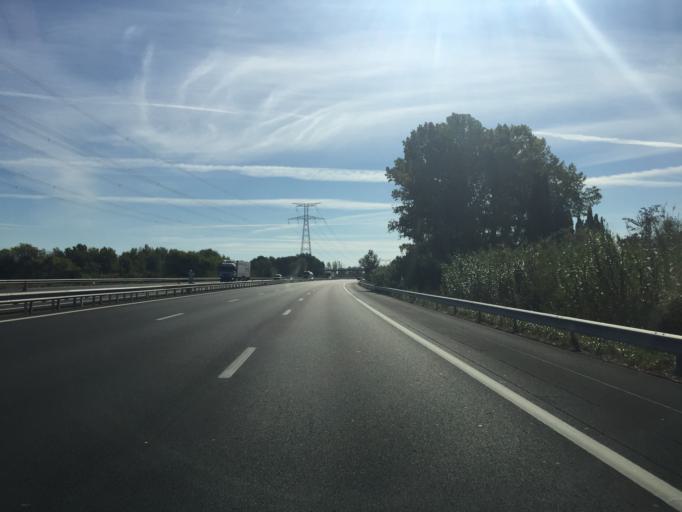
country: FR
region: Provence-Alpes-Cote d'Azur
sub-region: Departement des Bouches-du-Rhone
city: Cabannes
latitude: 43.8533
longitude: 4.9843
